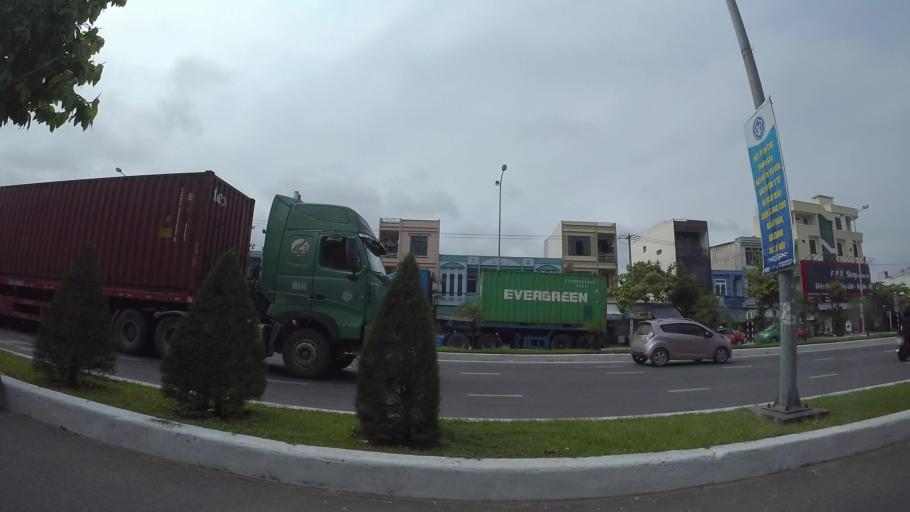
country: VN
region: Da Nang
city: Da Nang
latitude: 16.0785
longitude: 108.2324
